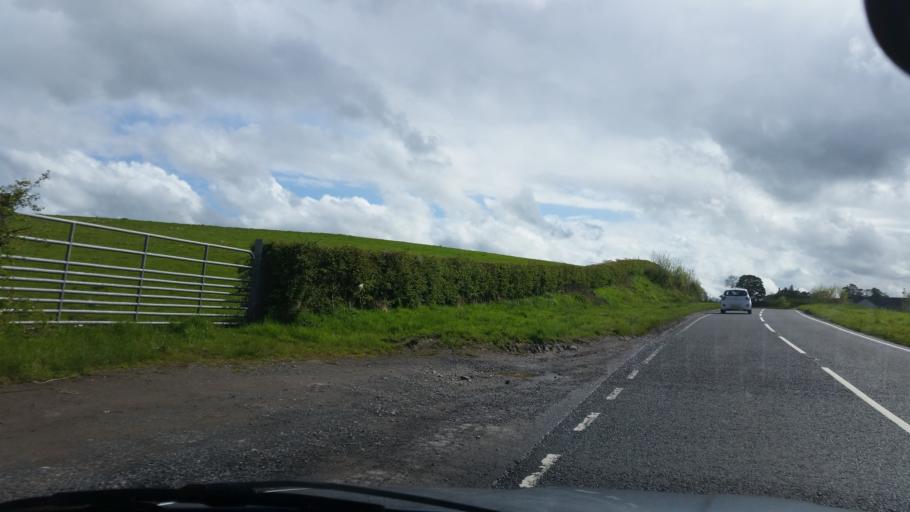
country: GB
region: Northern Ireland
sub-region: Omagh District
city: Omagh
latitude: 54.5611
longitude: -7.2765
